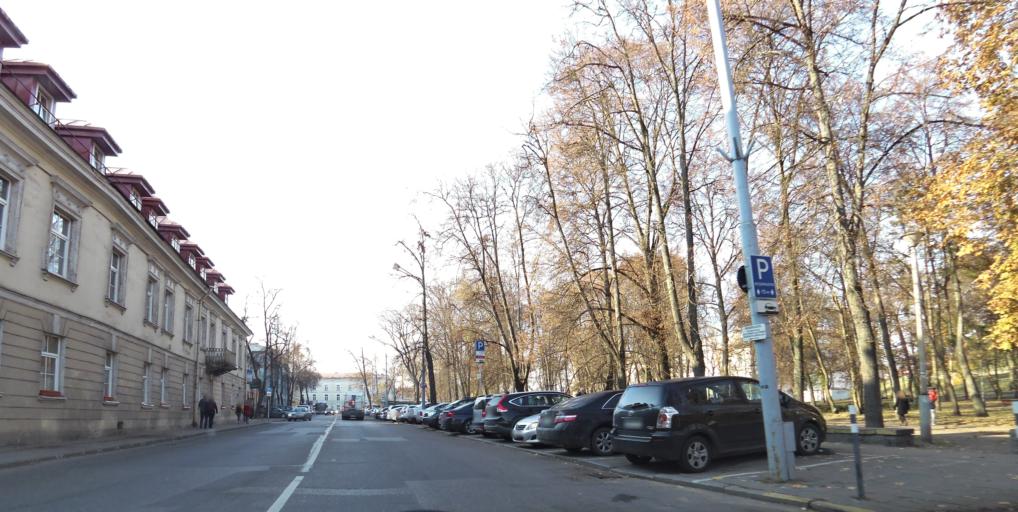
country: LT
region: Vilnius County
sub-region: Vilnius
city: Vilnius
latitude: 54.6852
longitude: 25.2924
